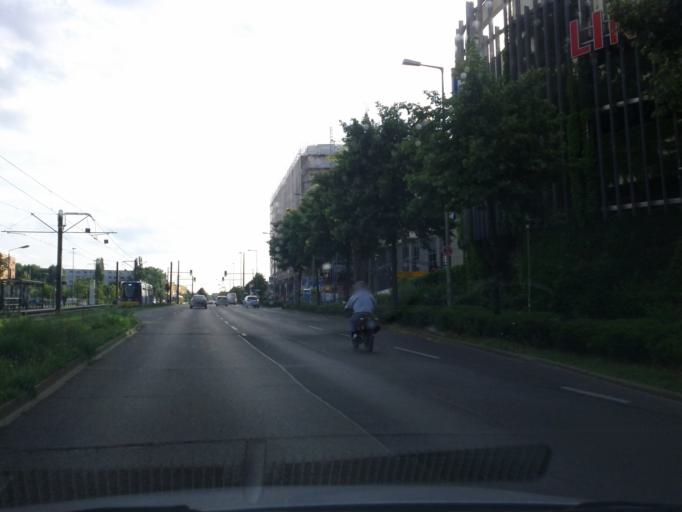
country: DE
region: Berlin
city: Neu-Hohenschoenhausen
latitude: 52.5641
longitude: 13.5072
